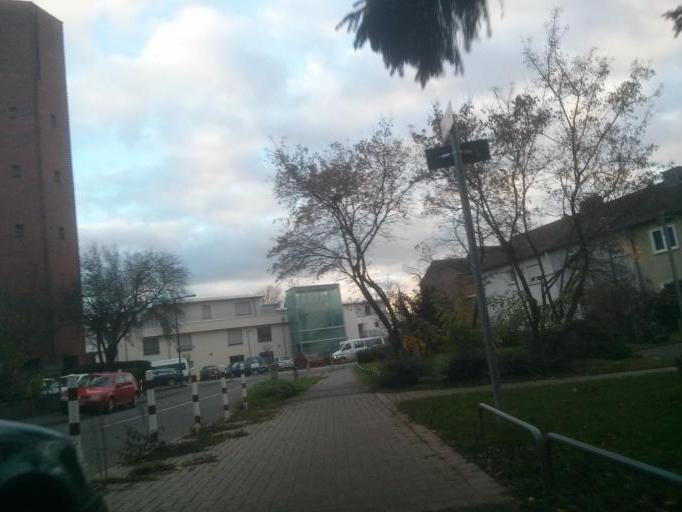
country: DE
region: North Rhine-Westphalia
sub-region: Regierungsbezirk Koln
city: Poll
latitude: 50.9201
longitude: 6.9900
